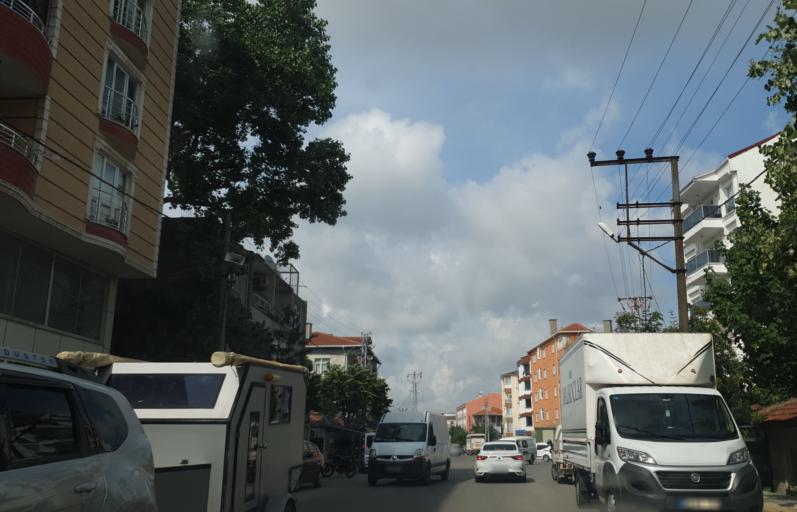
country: TR
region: Tekirdag
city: Saray
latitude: 41.4467
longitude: 27.9282
